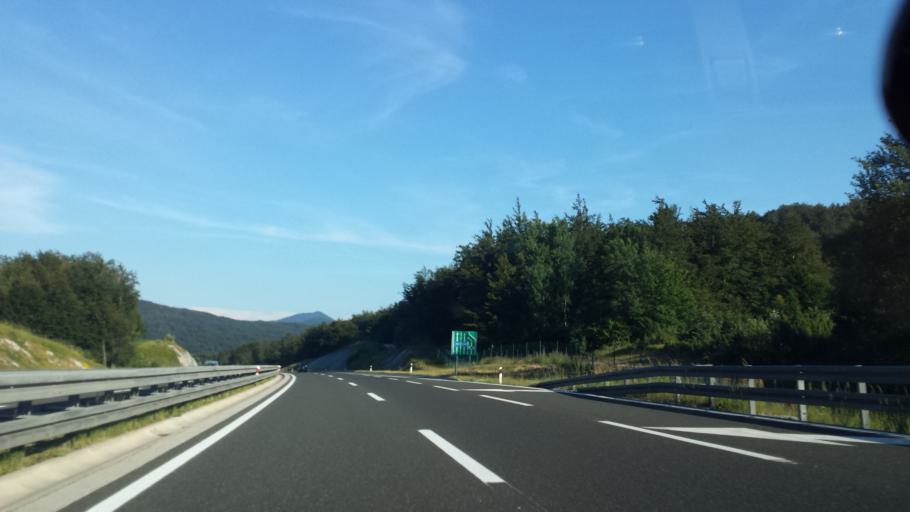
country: HR
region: Primorsko-Goranska
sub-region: Grad Delnice
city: Delnice
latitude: 45.3870
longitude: 14.8356
